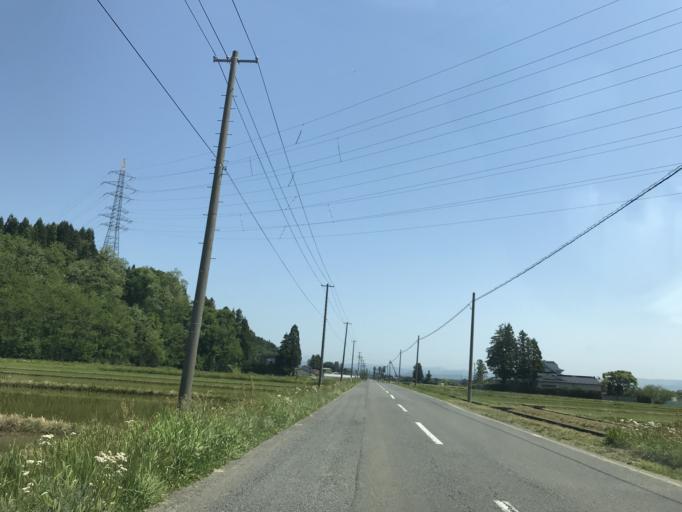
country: JP
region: Iwate
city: Mizusawa
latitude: 39.1635
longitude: 141.0788
